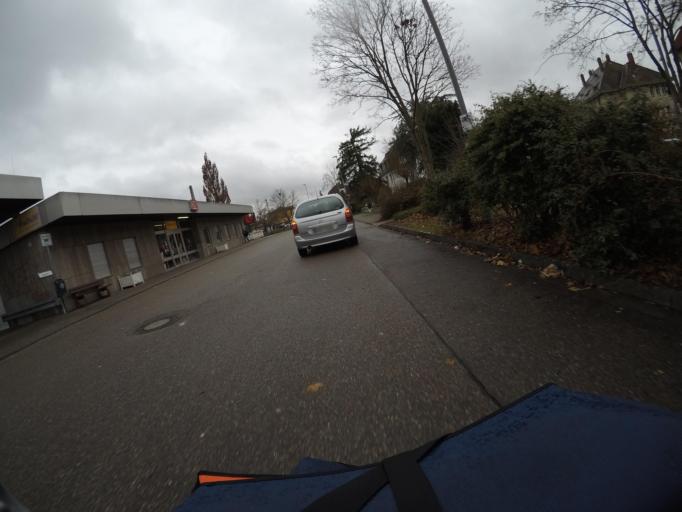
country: DE
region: Baden-Wuerttemberg
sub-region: Karlsruhe Region
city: Graben-Neudorf
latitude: 49.1625
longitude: 8.4901
